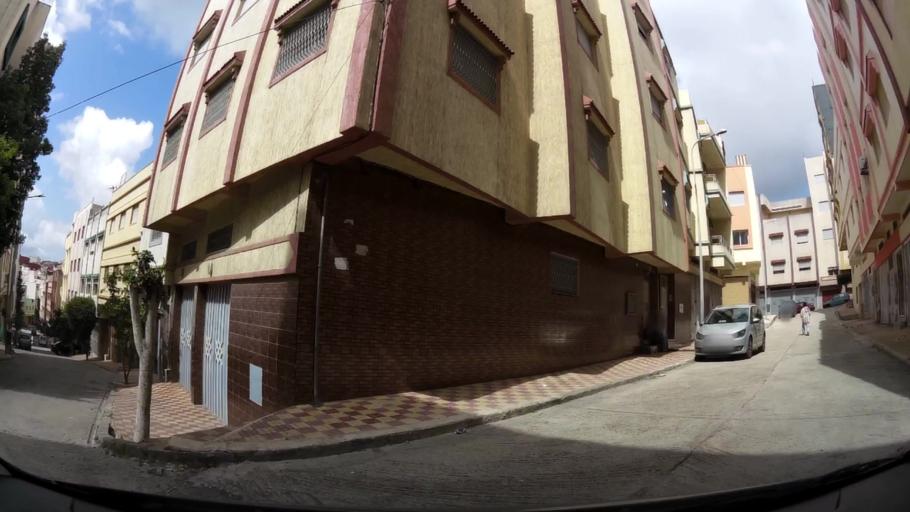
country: MA
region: Tanger-Tetouan
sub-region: Tanger-Assilah
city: Tangier
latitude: 35.7576
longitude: -5.8155
